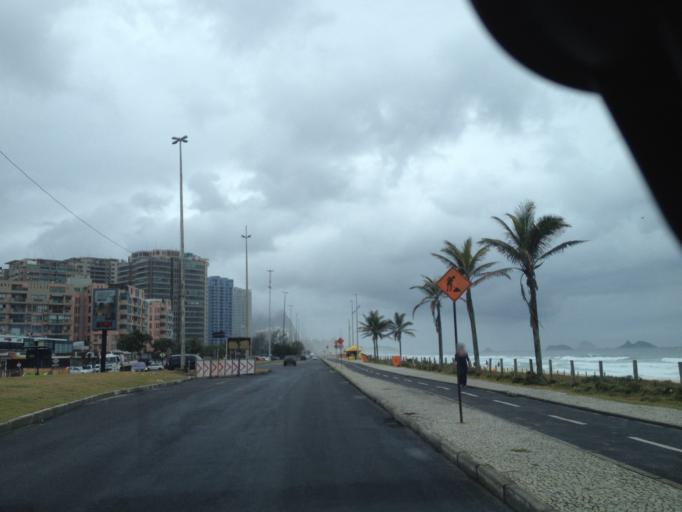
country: BR
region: Rio de Janeiro
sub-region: Rio De Janeiro
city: Rio de Janeiro
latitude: -23.0111
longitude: -43.3713
